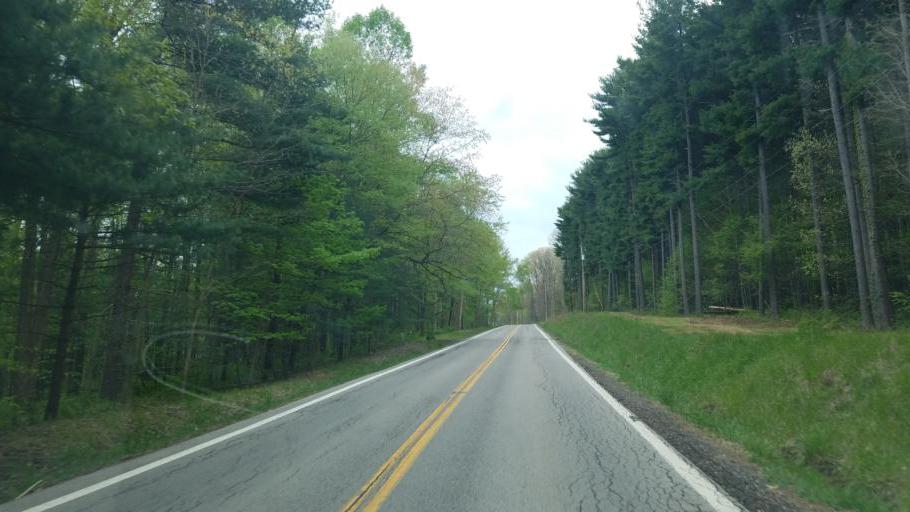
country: US
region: Ohio
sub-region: Ashland County
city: Loudonville
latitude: 40.6001
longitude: -82.3049
